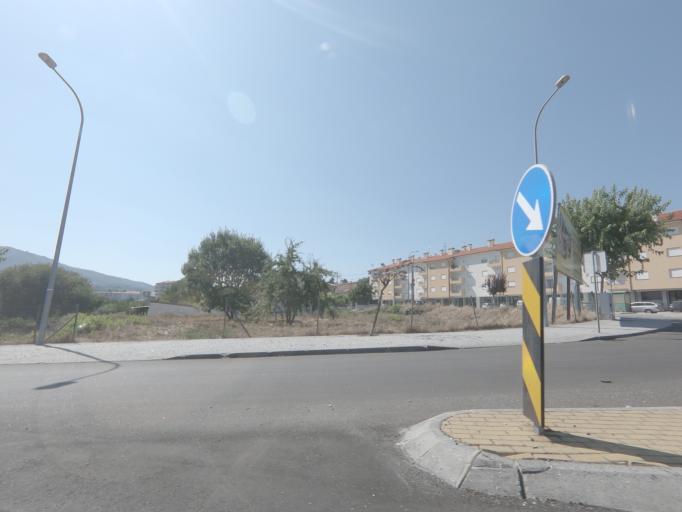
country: PT
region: Viseu
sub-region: Tarouca
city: Tarouca
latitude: 41.0276
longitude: -7.7634
